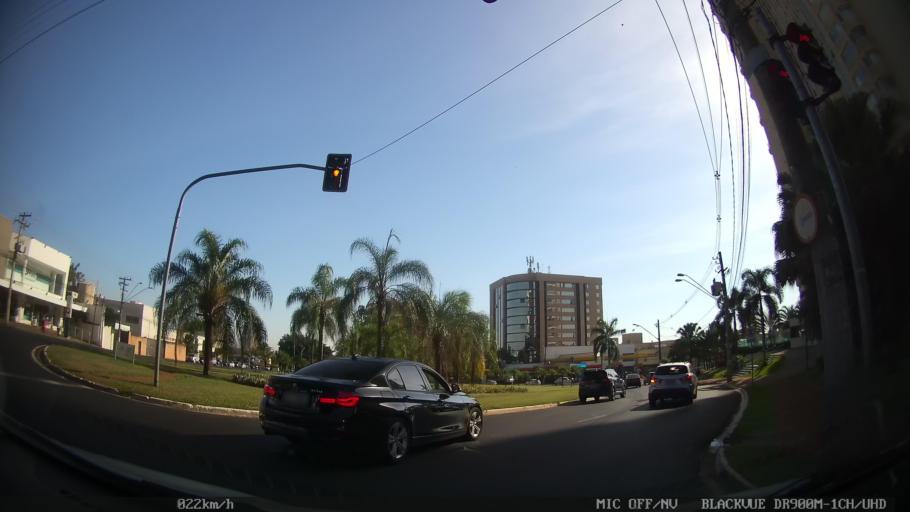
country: BR
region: Sao Paulo
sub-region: Ribeirao Preto
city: Ribeirao Preto
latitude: -21.2128
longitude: -47.8052
